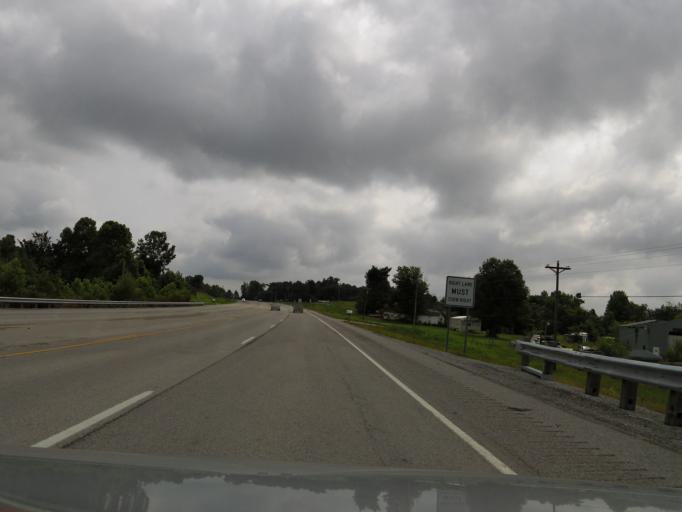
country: US
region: Kentucky
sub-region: Hopkins County
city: Madisonville
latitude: 37.3338
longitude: -87.4206
